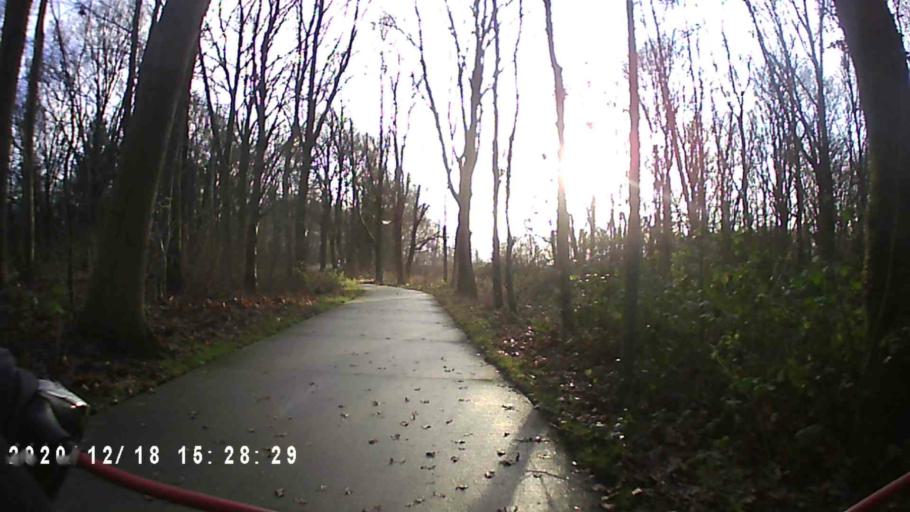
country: NL
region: Groningen
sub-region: Gemeente Hoogezand-Sappemeer
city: Hoogezand
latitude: 53.1461
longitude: 6.7072
